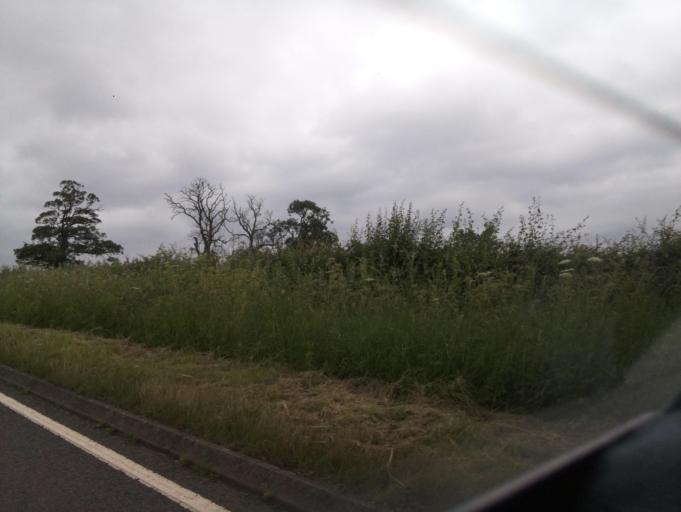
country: GB
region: England
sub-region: Leicestershire
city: Melton Mowbray
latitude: 52.7208
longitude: -0.8343
